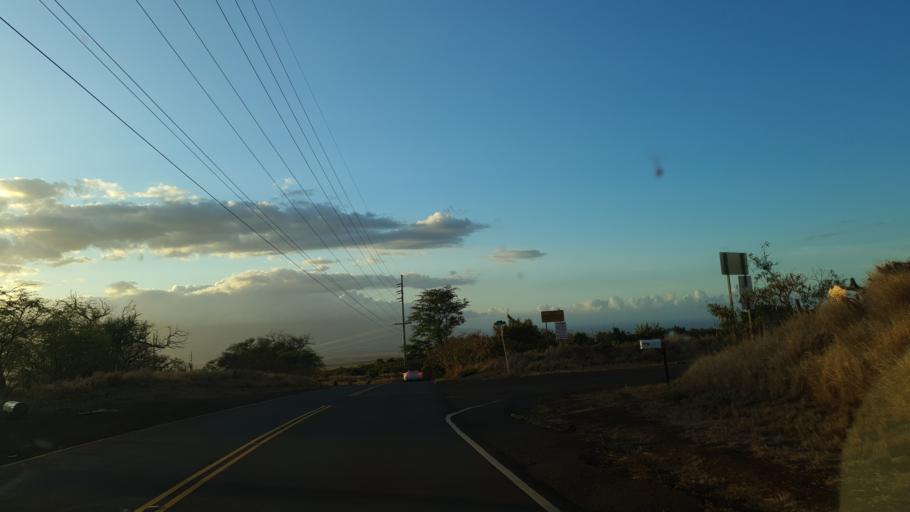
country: US
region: Hawaii
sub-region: Maui County
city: Pukalani
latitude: 20.7936
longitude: -156.3639
